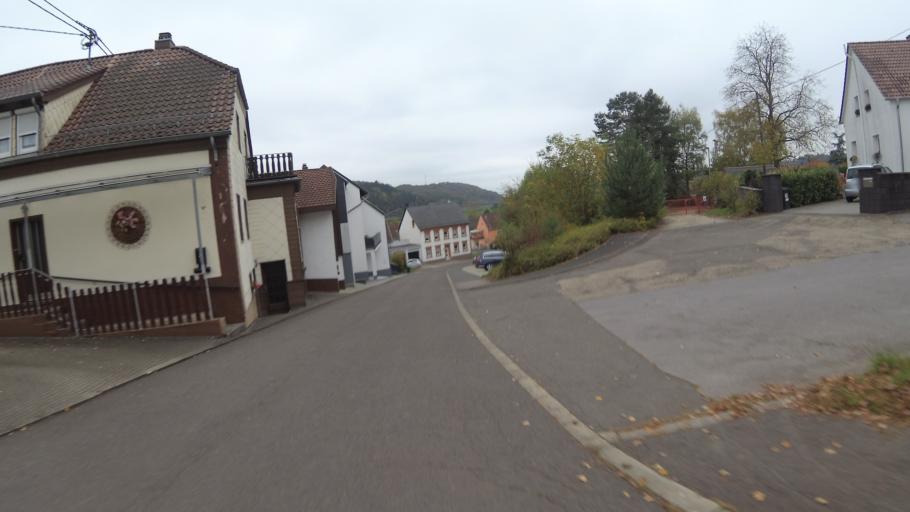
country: DE
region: Saarland
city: Blieskastel
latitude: 49.2637
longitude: 7.2850
